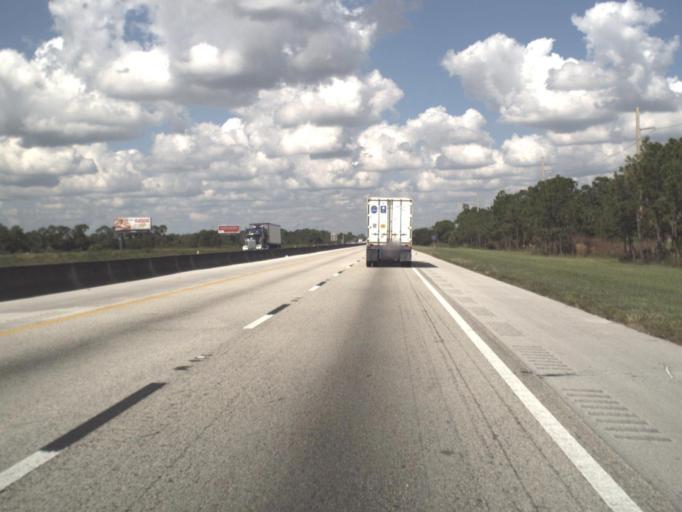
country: US
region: Florida
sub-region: Martin County
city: Palm City
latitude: 27.1689
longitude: -80.3096
